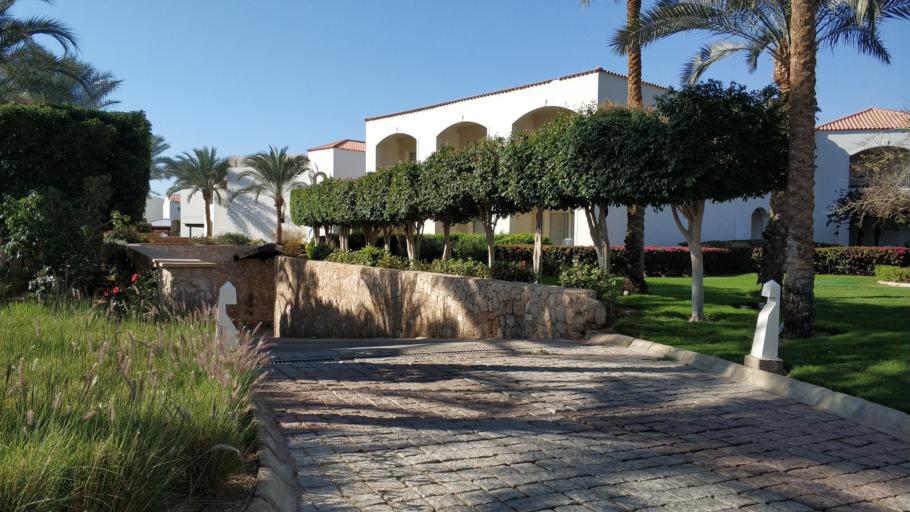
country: EG
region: South Sinai
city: Sharm el-Sheikh
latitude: 27.9208
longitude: 34.3616
